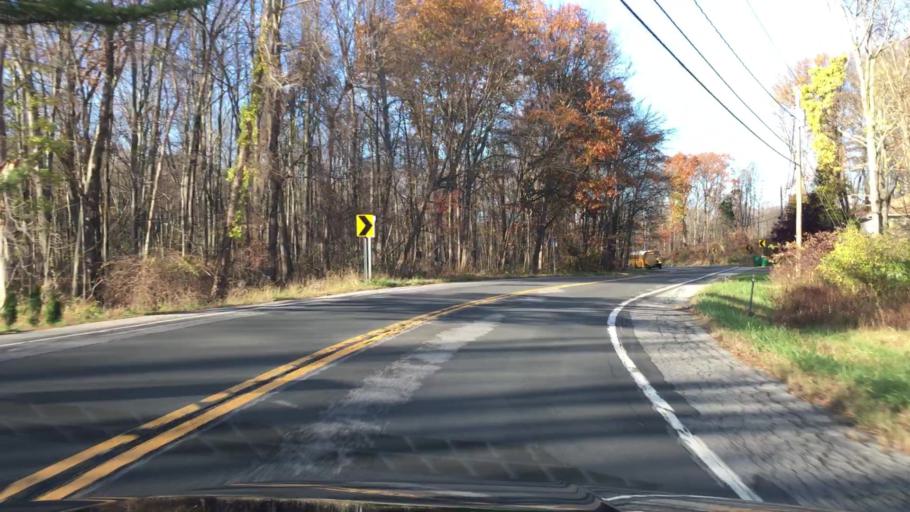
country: US
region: New York
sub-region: Dutchess County
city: Myers Corner
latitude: 41.6162
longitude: -73.8501
